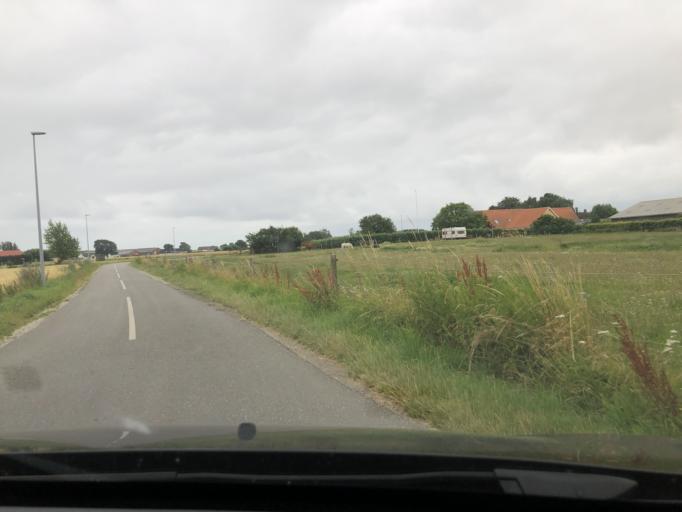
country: DK
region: South Denmark
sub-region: AEro Kommune
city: Marstal
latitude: 54.8517
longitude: 10.4758
